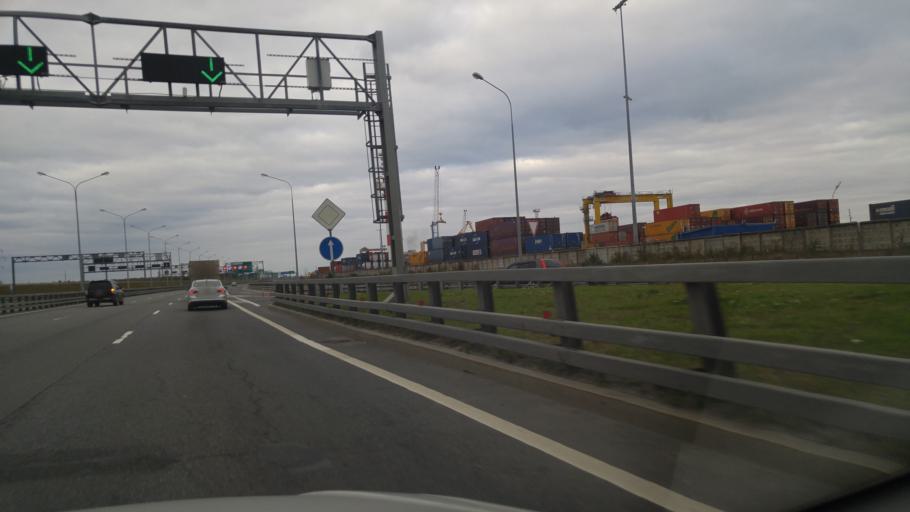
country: RU
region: St.-Petersburg
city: Kronshtadt
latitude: 59.9999
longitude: 29.7021
